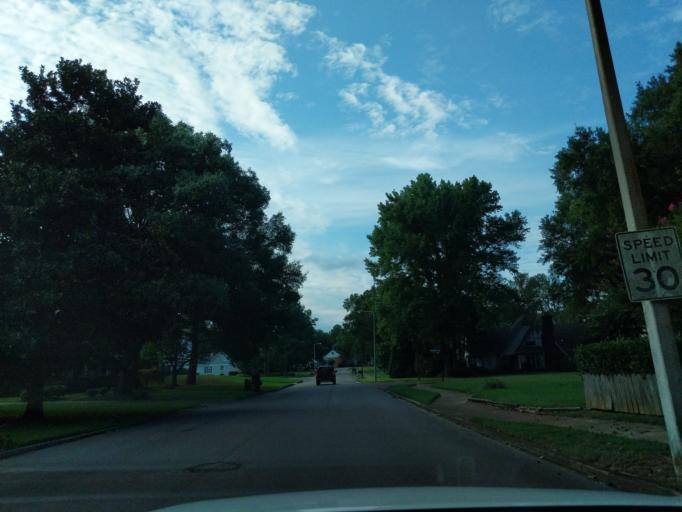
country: US
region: Tennessee
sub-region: Shelby County
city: Germantown
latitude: 35.0699
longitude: -89.7859
